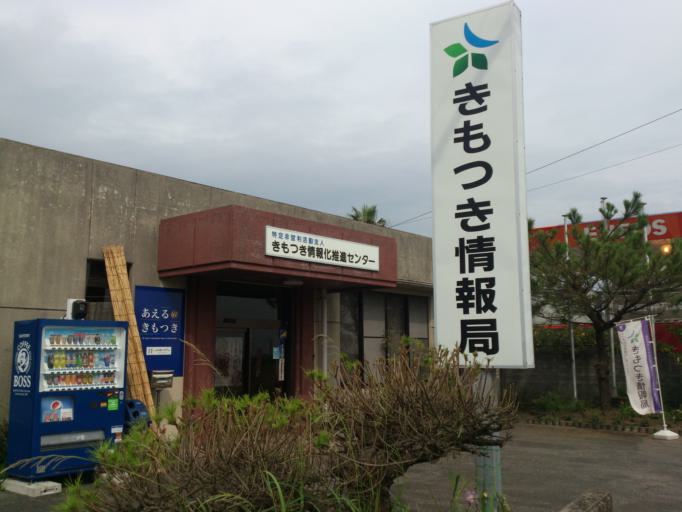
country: JP
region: Kagoshima
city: Kanoya
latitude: 31.3531
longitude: 130.9388
